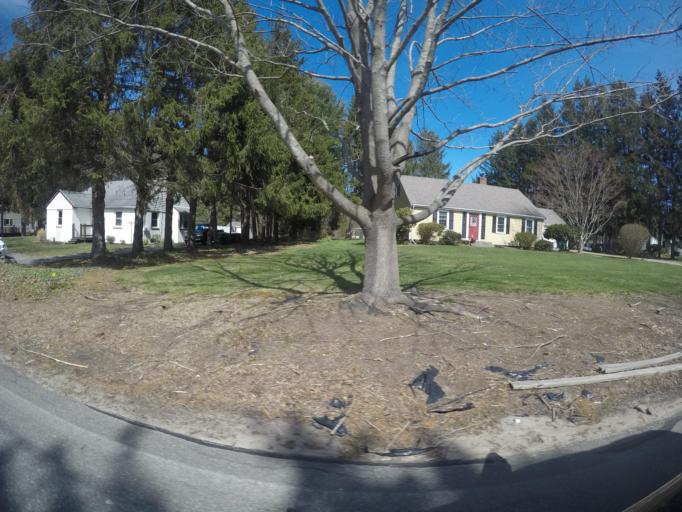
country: US
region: Massachusetts
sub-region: Bristol County
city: Easton
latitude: 42.0255
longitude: -71.0827
